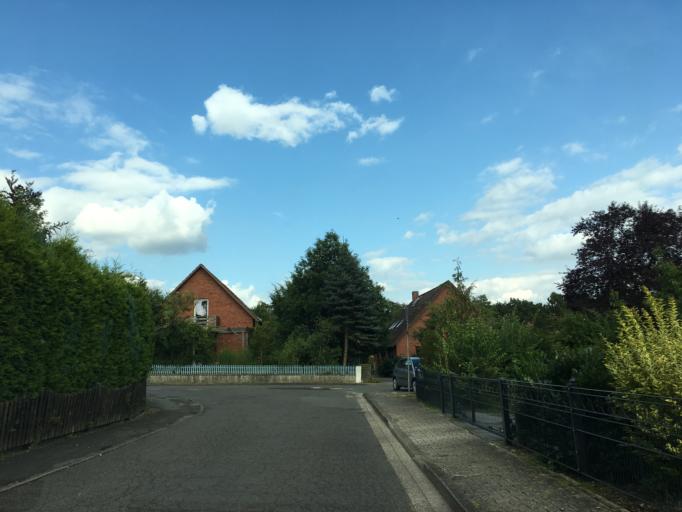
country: DE
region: Lower Saxony
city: Melbeck
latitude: 53.2180
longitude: 10.3859
